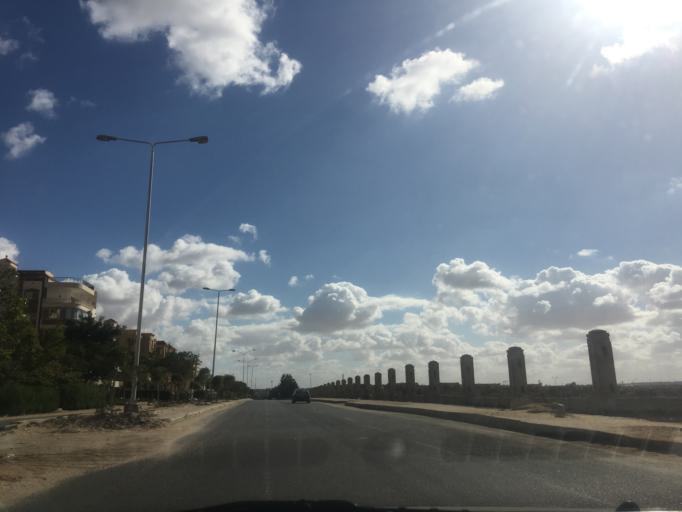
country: EG
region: Al Jizah
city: Madinat Sittah Uktubar
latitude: 30.0011
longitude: 30.9736
